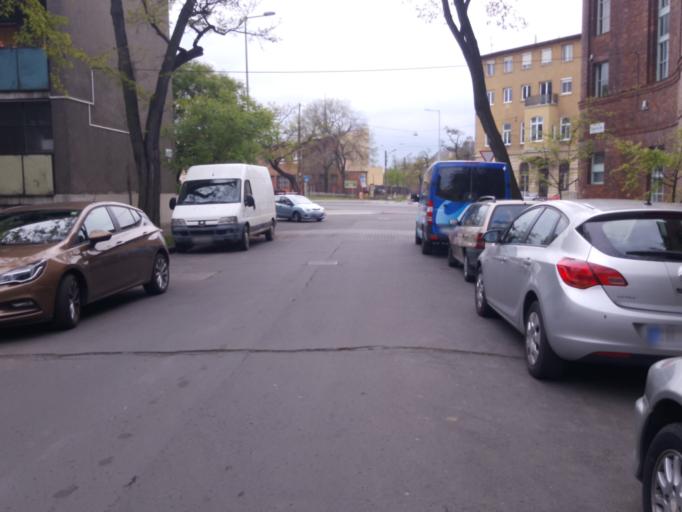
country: HU
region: Budapest
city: Budapest X. keruelet
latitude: 47.4823
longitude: 19.1324
